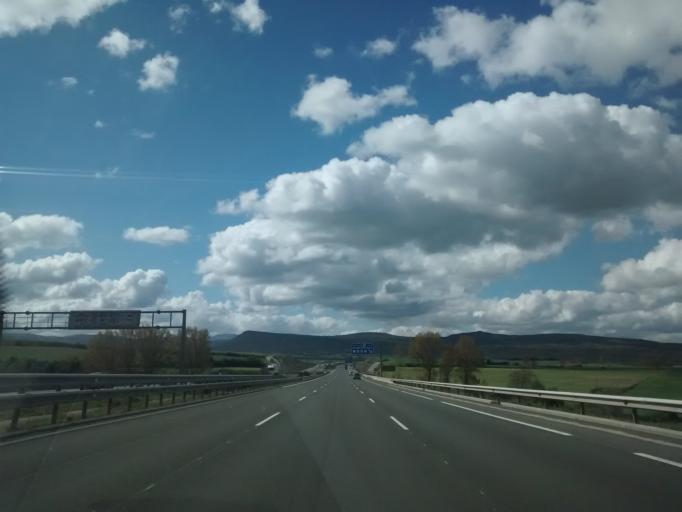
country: ES
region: Basque Country
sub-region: Provincia de Alava
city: Arminon
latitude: 42.7742
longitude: -2.8235
